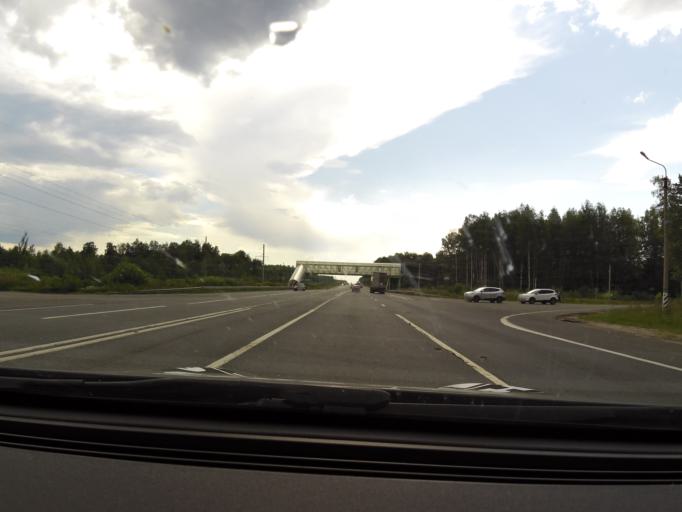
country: RU
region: Nizjnij Novgorod
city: Smolino
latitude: 56.2819
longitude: 43.0946
